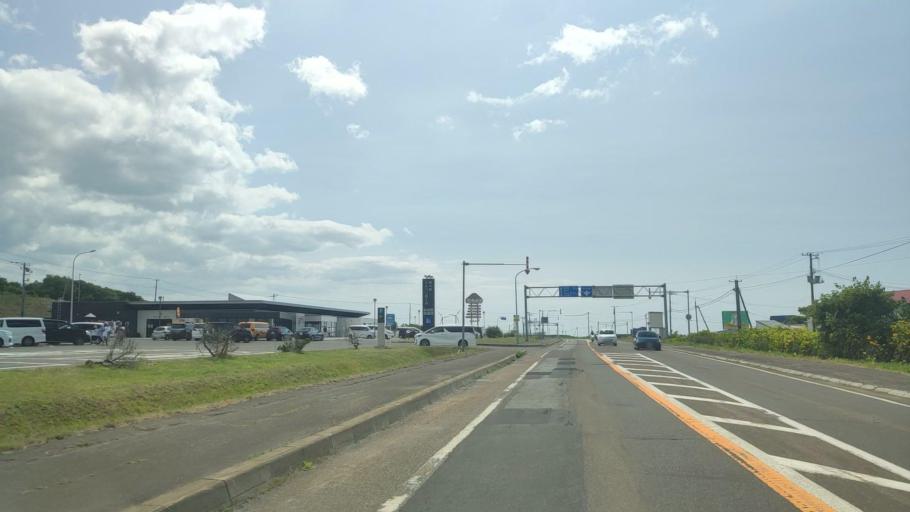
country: JP
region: Hokkaido
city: Makubetsu
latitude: 44.7145
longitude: 141.7920
